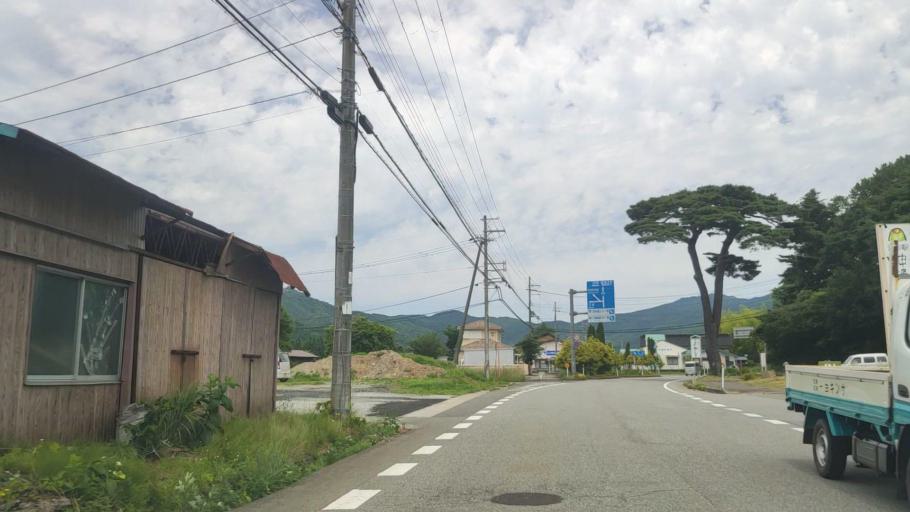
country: JP
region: Hyogo
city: Toyooka
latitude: 35.4990
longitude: 134.6743
